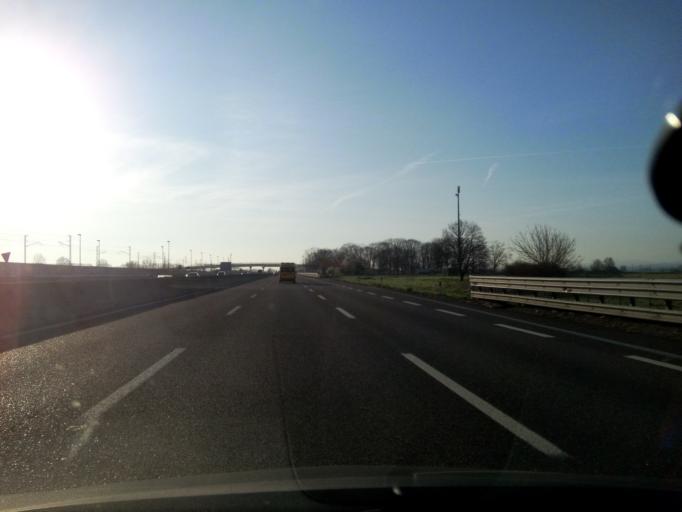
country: IT
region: Emilia-Romagna
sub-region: Provincia di Piacenza
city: Alseno
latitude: 44.9333
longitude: 9.9723
